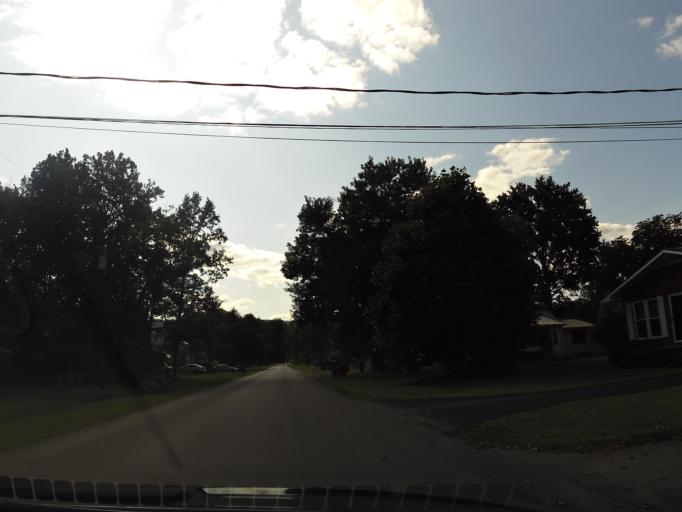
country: US
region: Kentucky
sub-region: Bell County
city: Middlesboro
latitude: 36.6022
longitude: -83.7202
